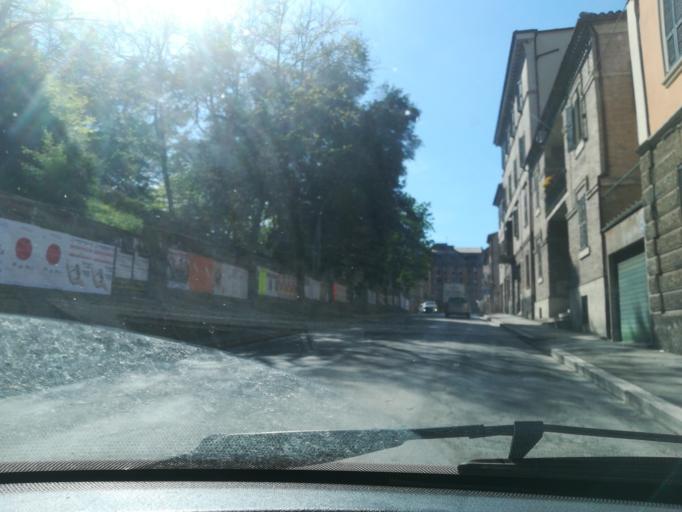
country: IT
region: The Marches
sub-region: Provincia di Macerata
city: Macerata
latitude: 43.2957
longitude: 13.4582
